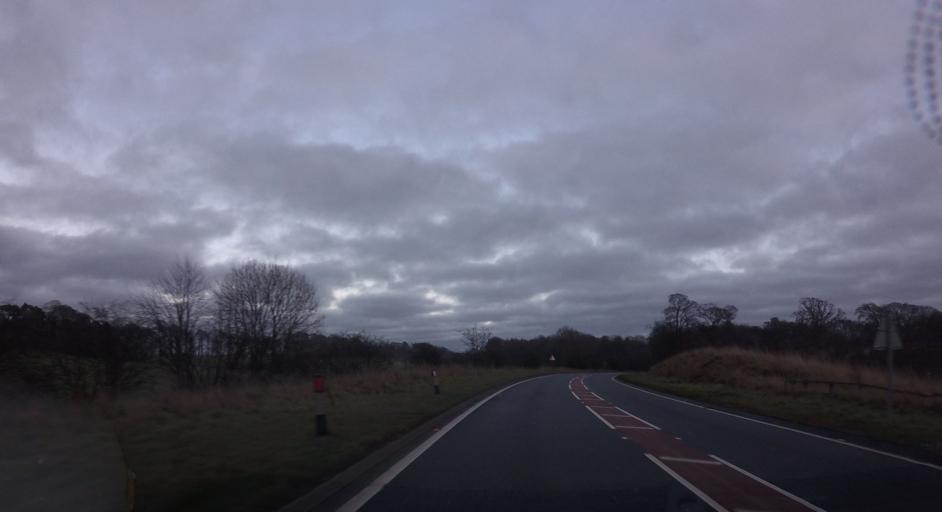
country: GB
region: Scotland
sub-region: Fife
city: Limekilns
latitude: 56.0461
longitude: -3.4803
